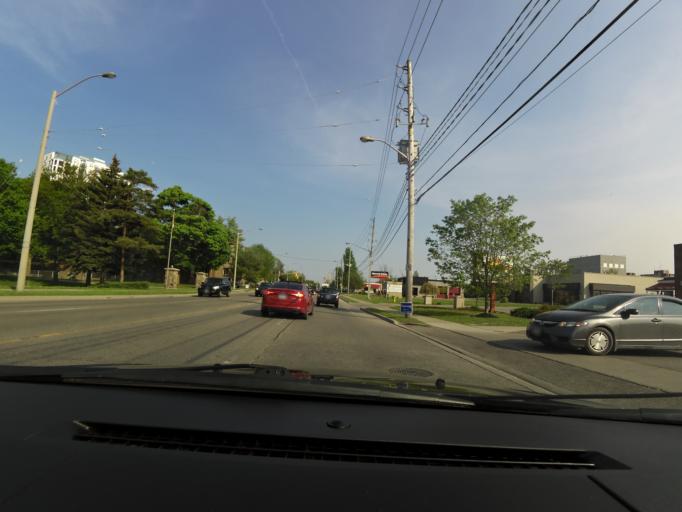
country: CA
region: Ontario
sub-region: Wellington County
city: Guelph
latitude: 43.5612
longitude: -80.2722
